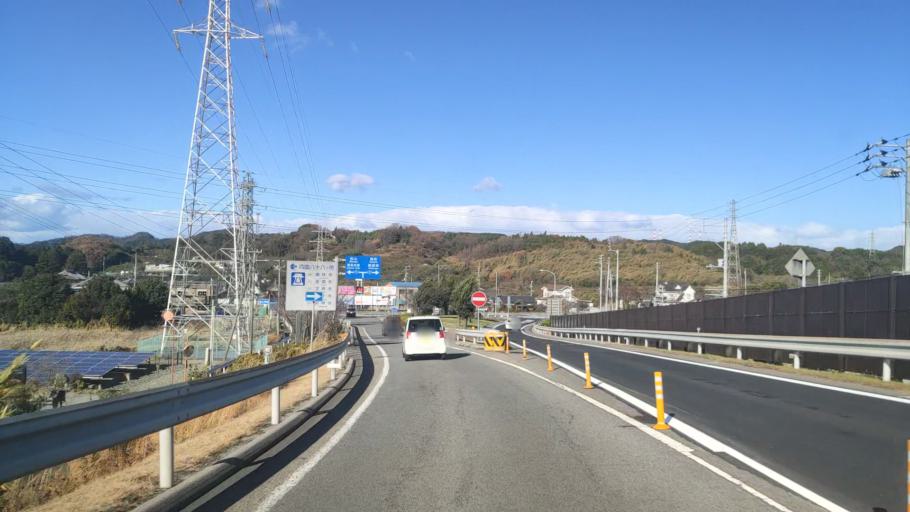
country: JP
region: Ehime
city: Saijo
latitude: 33.9182
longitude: 133.2404
